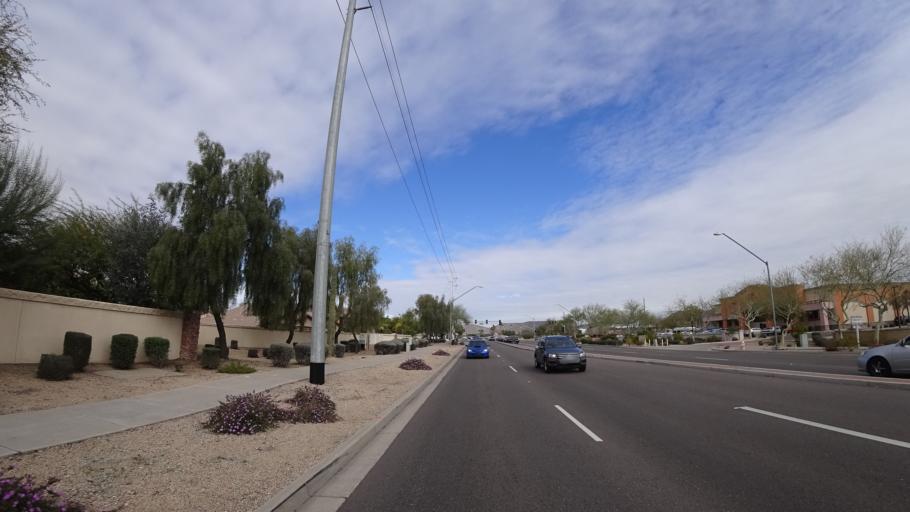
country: US
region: Arizona
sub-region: Maricopa County
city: Peoria
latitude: 33.6532
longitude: -112.1864
